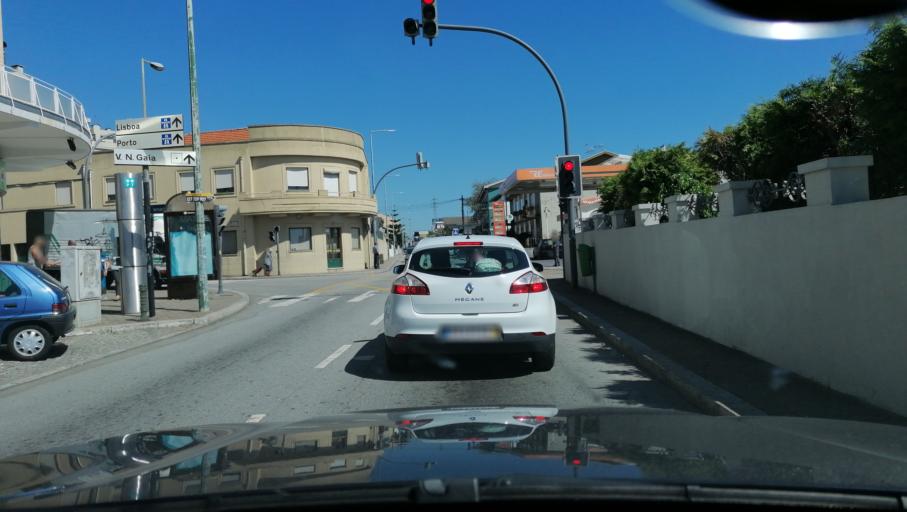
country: PT
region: Porto
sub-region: Vila Nova de Gaia
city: Canidelo
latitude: 41.1278
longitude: -8.6402
